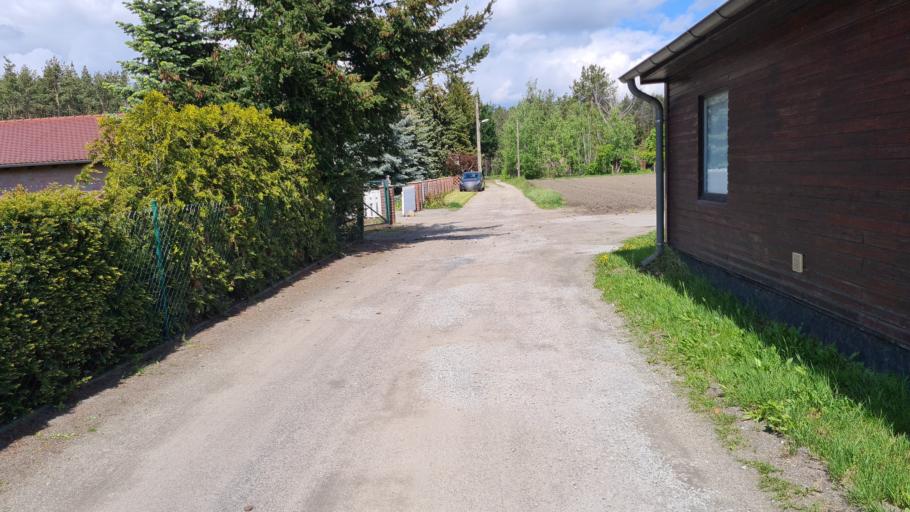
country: DE
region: Brandenburg
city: Grossraschen
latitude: 51.5882
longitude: 14.0340
